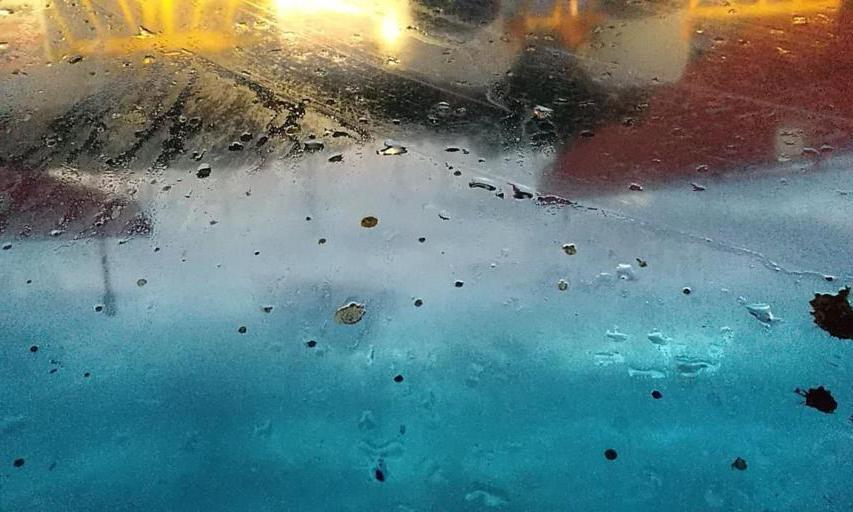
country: BR
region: Para
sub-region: Altamira
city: Altamira
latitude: -3.1230
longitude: -51.7001
